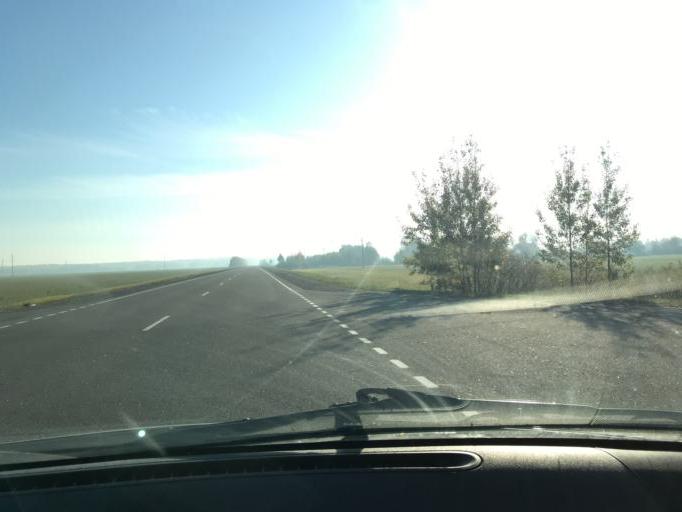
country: BY
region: Brest
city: Horad Luninyets
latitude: 52.3148
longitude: 26.6452
